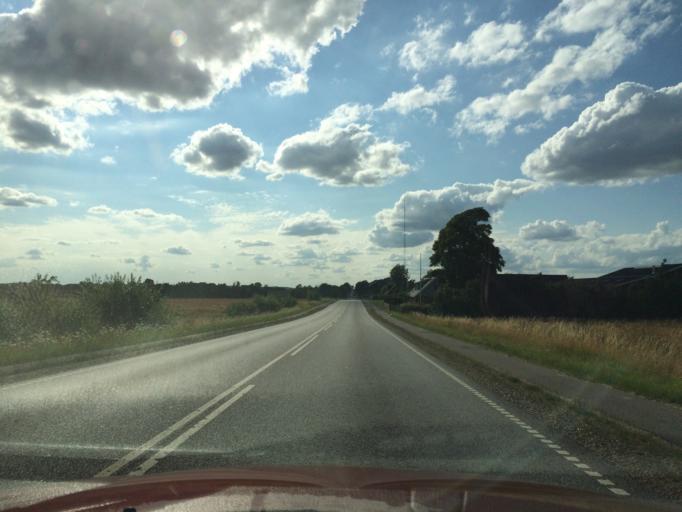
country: DK
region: Central Jutland
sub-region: Favrskov Kommune
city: Hammel
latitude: 56.2352
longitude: 9.8484
